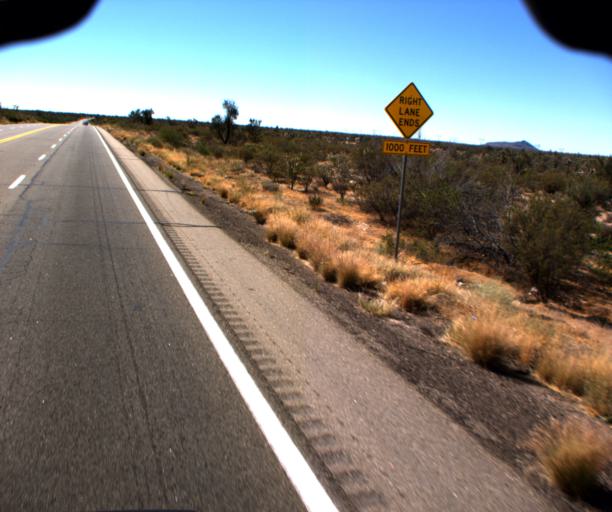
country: US
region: Arizona
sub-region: Yavapai County
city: Congress
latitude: 34.2782
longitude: -113.1006
